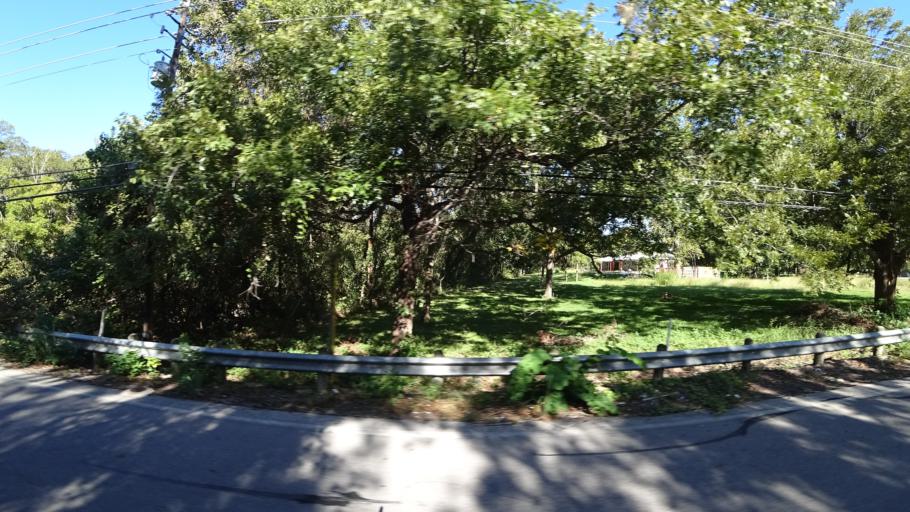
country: US
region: Texas
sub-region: Travis County
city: Manor
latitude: 30.3375
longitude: -97.6500
